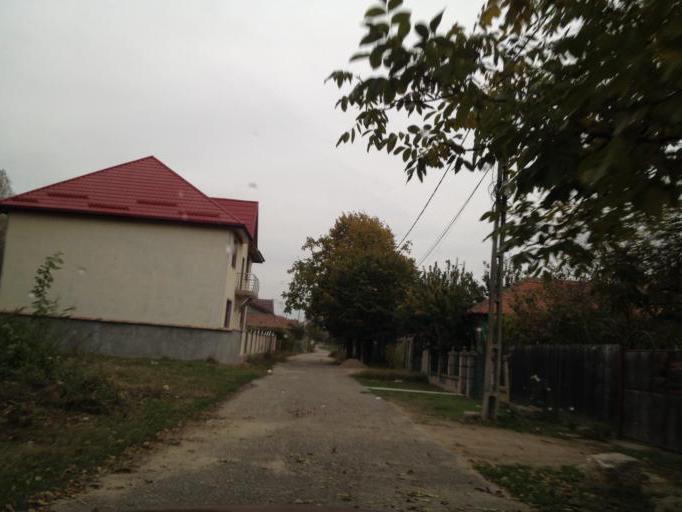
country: RO
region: Dolj
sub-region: Municipiul Craiova
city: Mofleni
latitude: 44.2980
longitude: 23.7576
